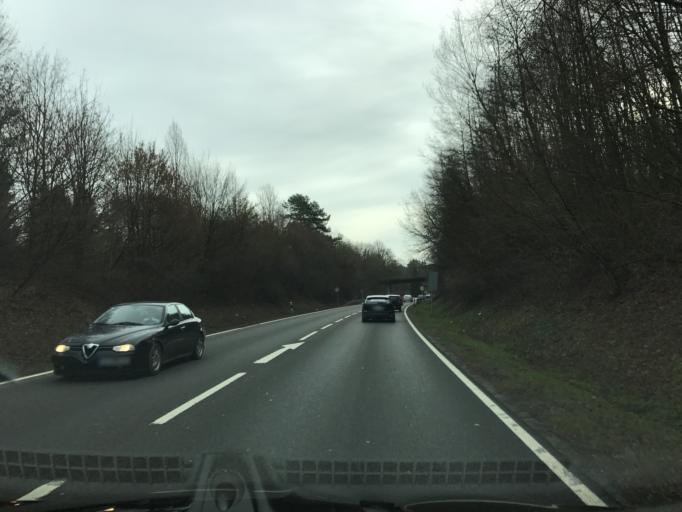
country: DE
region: Bavaria
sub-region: Swabia
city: Weissensberg
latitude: 47.5764
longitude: 9.7061
